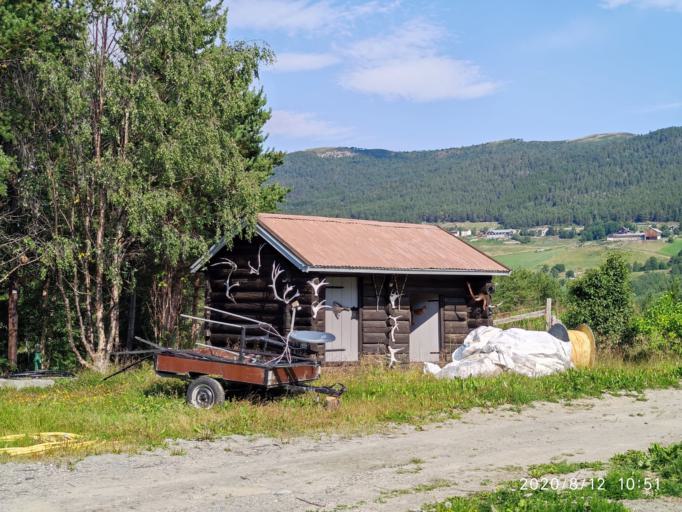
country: NO
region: Oppland
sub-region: Dovre
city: Dombas
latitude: 62.0823
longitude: 9.0611
